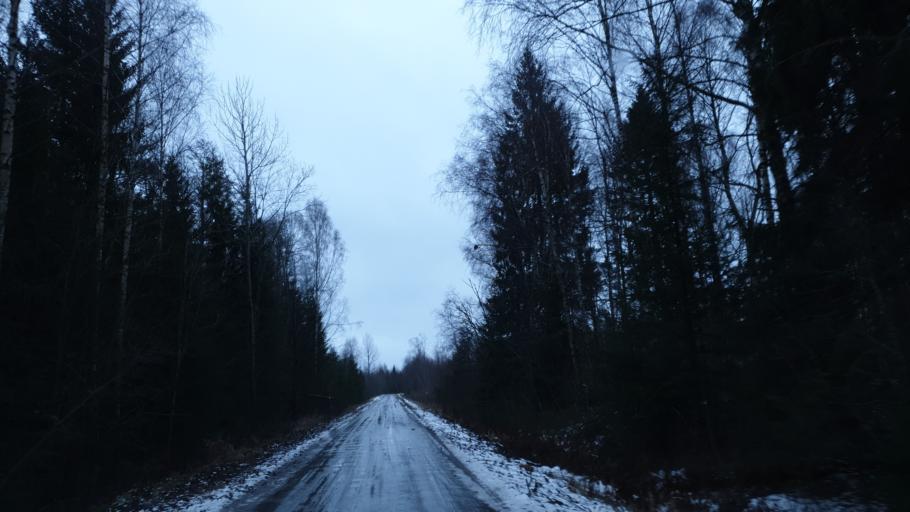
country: SE
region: Uppsala
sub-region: Tierps Kommun
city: Tierp
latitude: 60.3485
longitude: 17.4646
